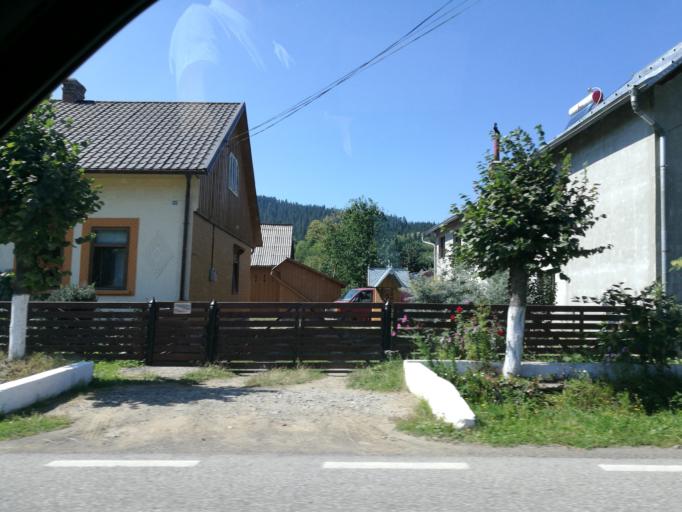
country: RO
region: Suceava
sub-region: Comuna Putna
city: Putna
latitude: 47.8771
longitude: 25.6148
